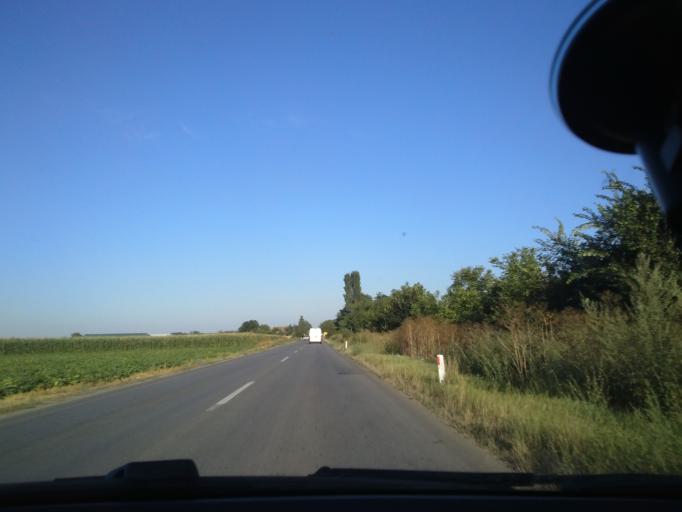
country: RS
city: Maglic
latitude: 45.3989
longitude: 19.4473
